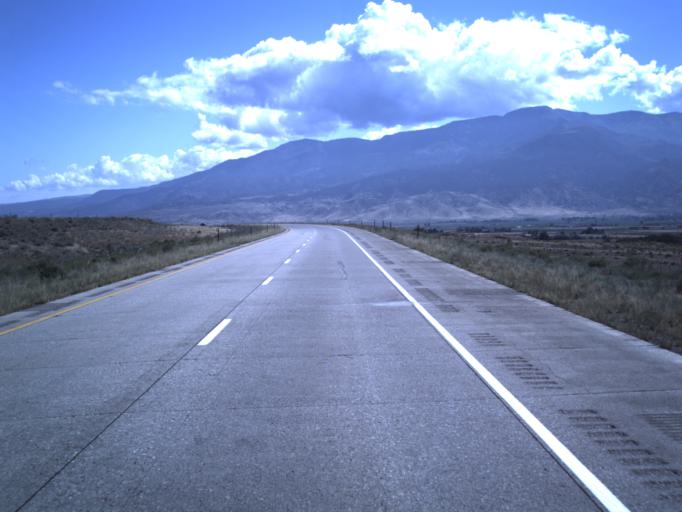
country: US
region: Utah
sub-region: Sevier County
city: Monroe
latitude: 38.6583
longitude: -112.1894
